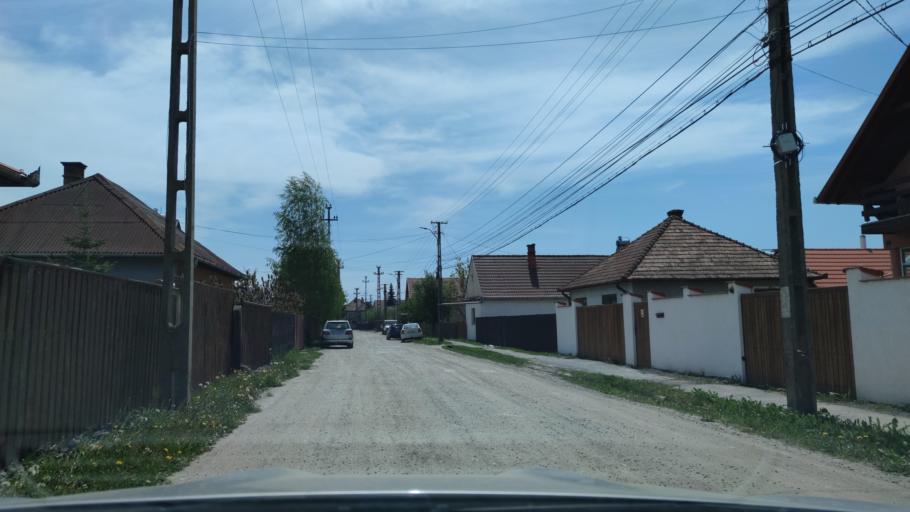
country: RO
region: Harghita
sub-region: Municipiul Gheorgheni
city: Gheorgheni
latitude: 46.7182
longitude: 25.5827
